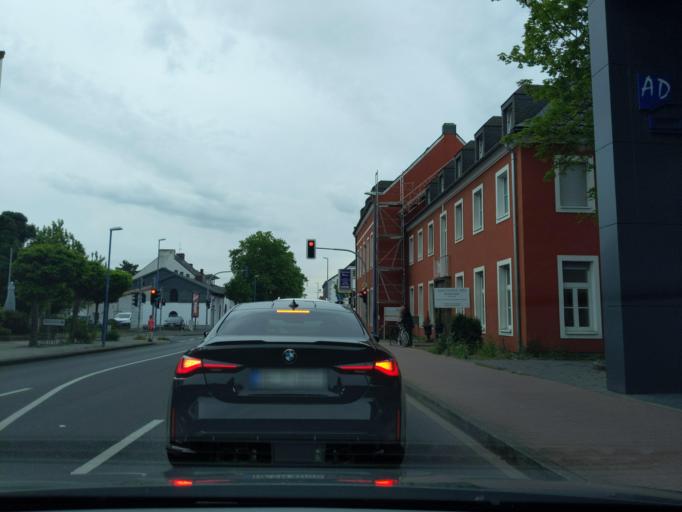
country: DE
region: North Rhine-Westphalia
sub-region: Regierungsbezirk Dusseldorf
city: Meerbusch
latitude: 51.2487
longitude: 6.6923
